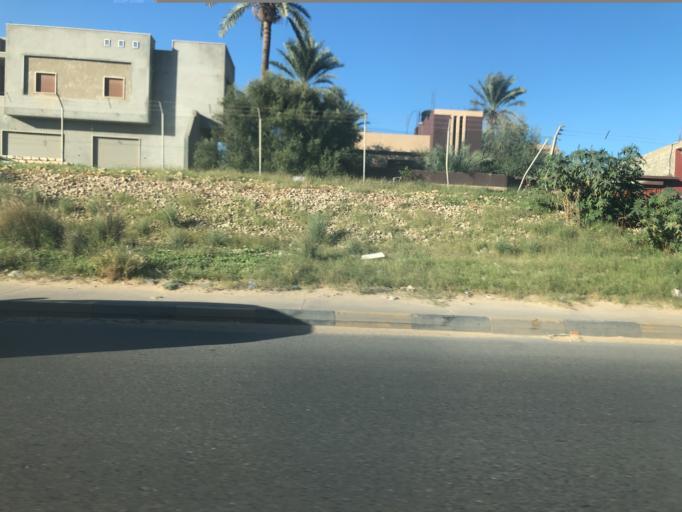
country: LY
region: Tripoli
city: Tagiura
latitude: 32.8692
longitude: 13.2796
